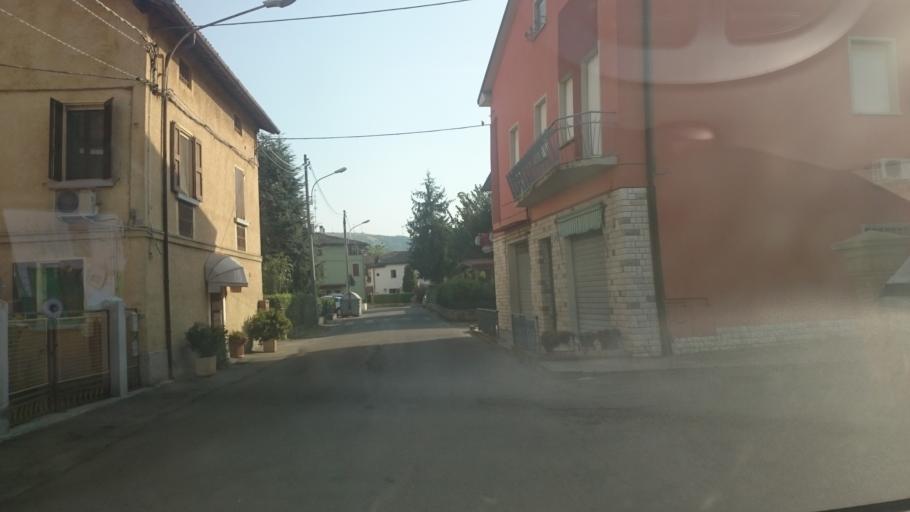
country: IT
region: Emilia-Romagna
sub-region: Provincia di Reggio Emilia
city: Scandiano
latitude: 44.5967
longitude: 10.7075
